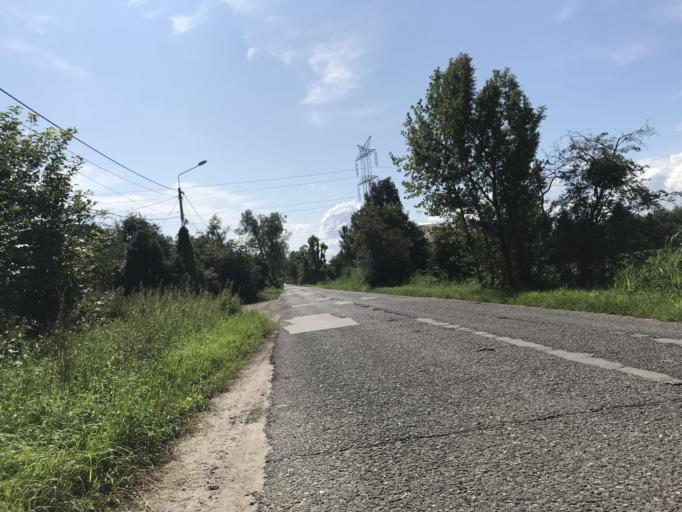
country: PL
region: Pomeranian Voivodeship
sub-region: Gdansk
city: Gdansk
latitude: 54.3212
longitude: 18.6788
